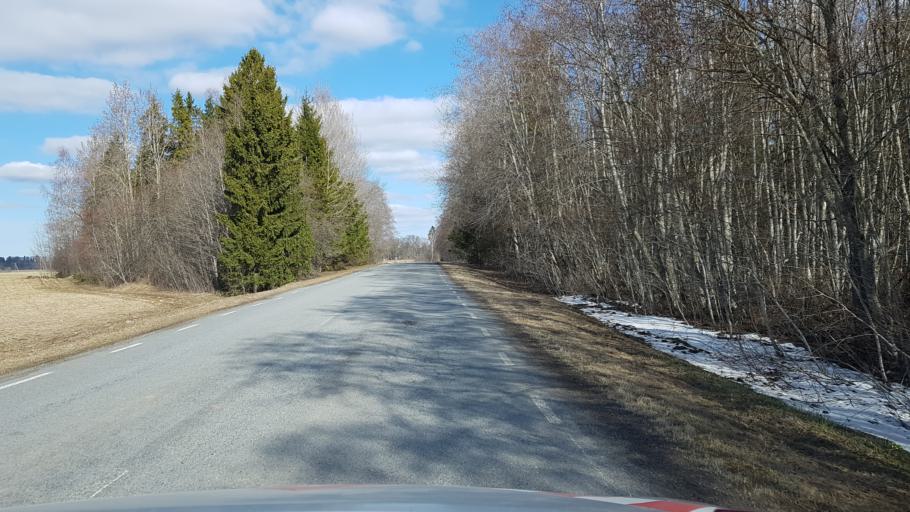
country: EE
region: Laeaene-Virumaa
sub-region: Tamsalu vald
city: Tamsalu
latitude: 59.1849
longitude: 26.0238
